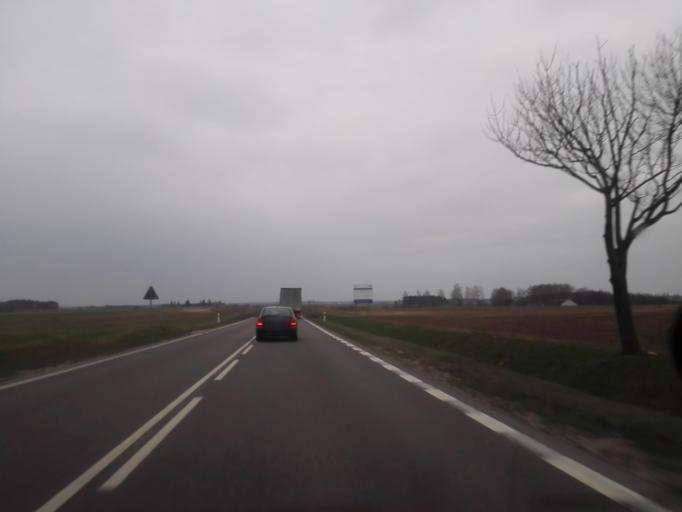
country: PL
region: Podlasie
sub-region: Powiat grajewski
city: Szczuczyn
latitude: 53.5833
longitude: 22.3238
